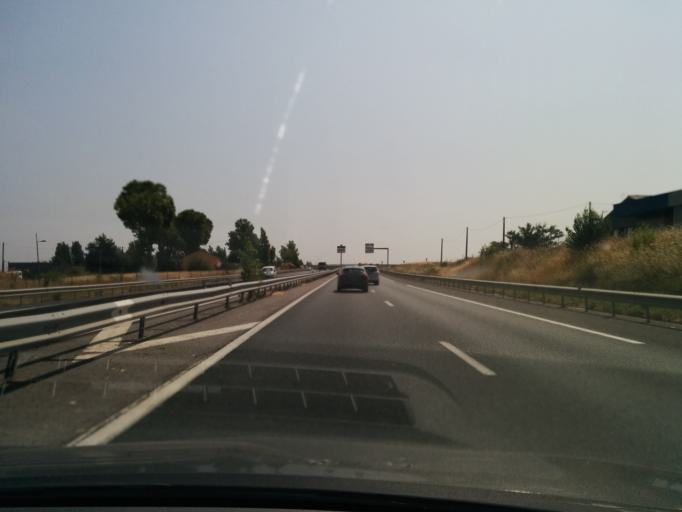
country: FR
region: Midi-Pyrenees
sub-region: Departement du Tarn
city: Castelnau-de-Levis
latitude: 43.9162
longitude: 2.0824
